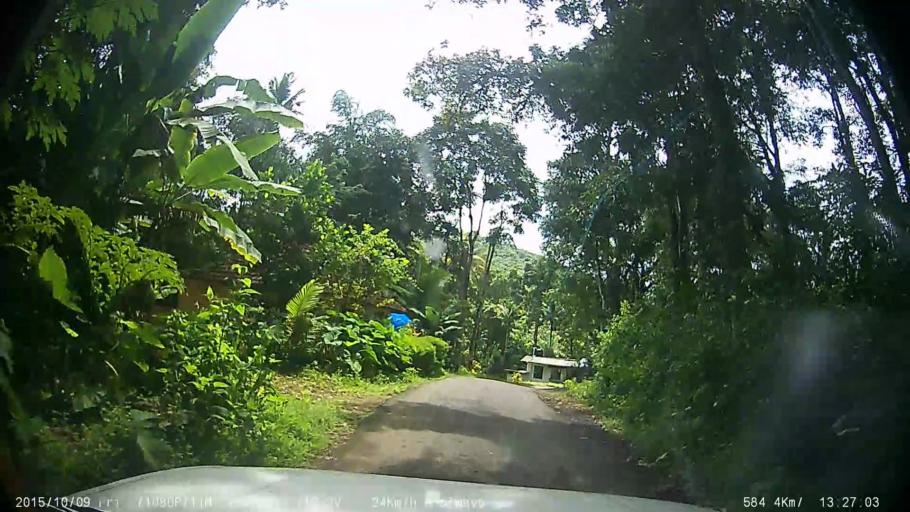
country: IN
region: Kerala
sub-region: Ernakulam
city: Muvattupuzha
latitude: 9.9202
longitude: 76.5616
